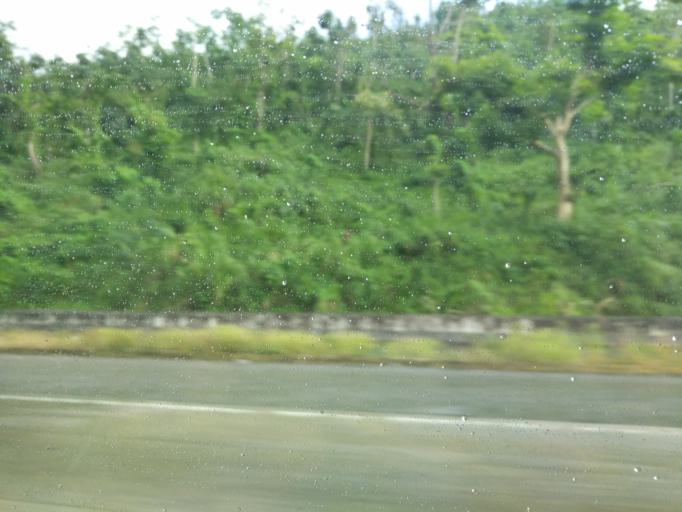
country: PR
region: Cidra
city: Bayamon
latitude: 18.1658
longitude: -66.0808
